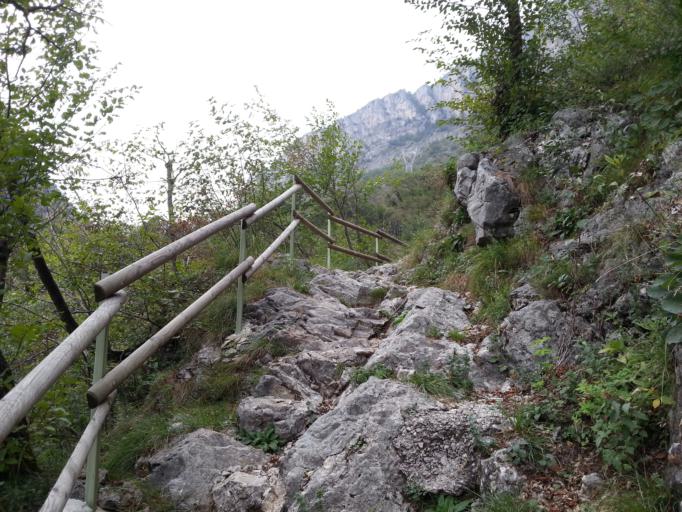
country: IT
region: Lombardy
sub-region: Provincia di Lecco
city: Ballabio
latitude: 45.8767
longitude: 9.4332
